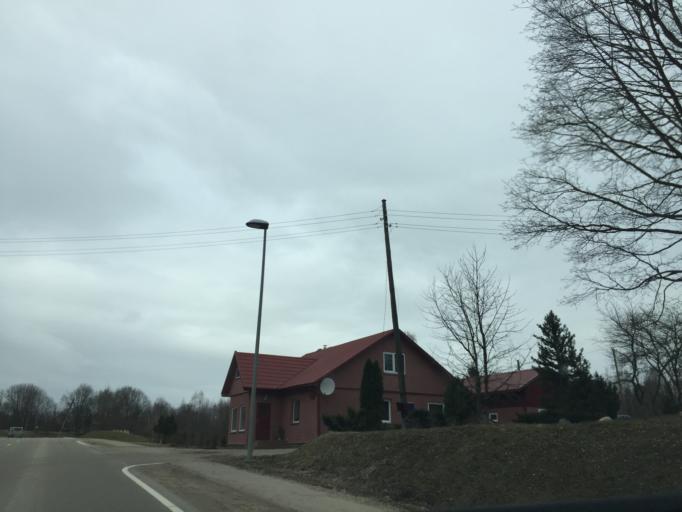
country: LV
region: Kraslavas Rajons
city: Kraslava
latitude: 55.9124
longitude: 27.1545
